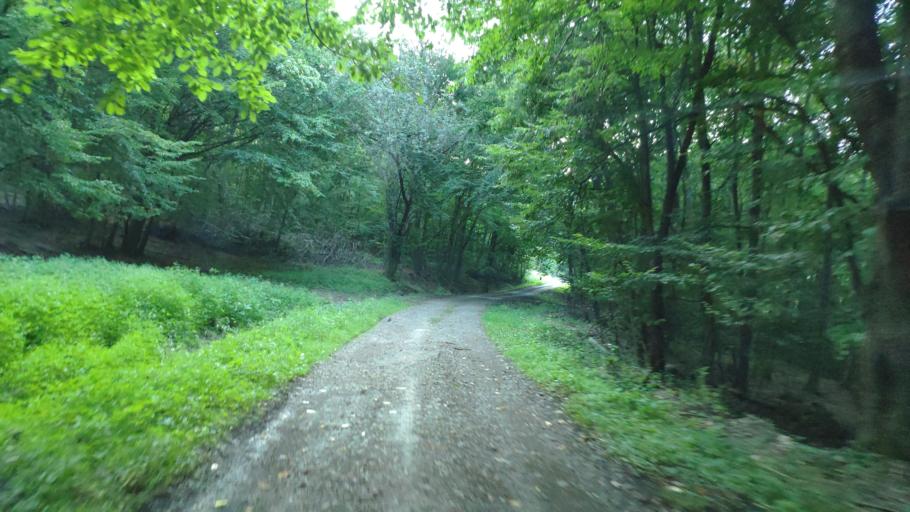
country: SK
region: Kosicky
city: Secovce
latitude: 48.5862
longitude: 21.5302
